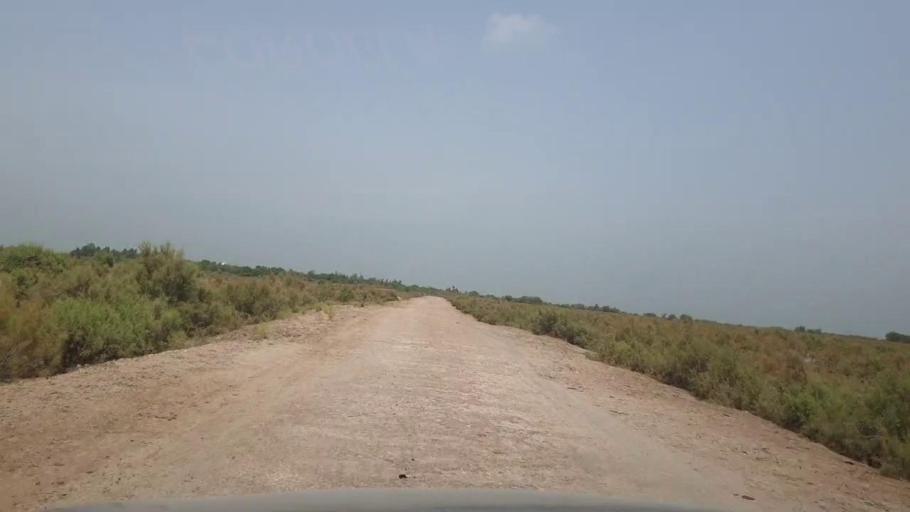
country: PK
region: Sindh
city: Garhi Yasin
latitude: 27.9153
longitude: 68.3784
